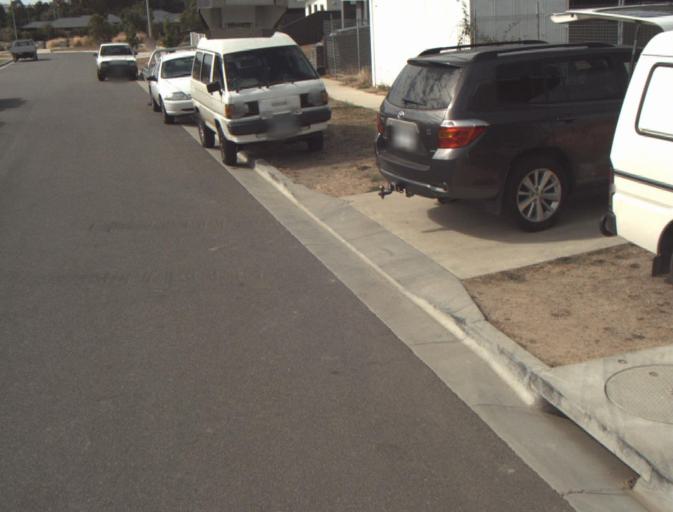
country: AU
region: Tasmania
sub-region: Launceston
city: Summerhill
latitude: -41.4663
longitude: 147.1354
